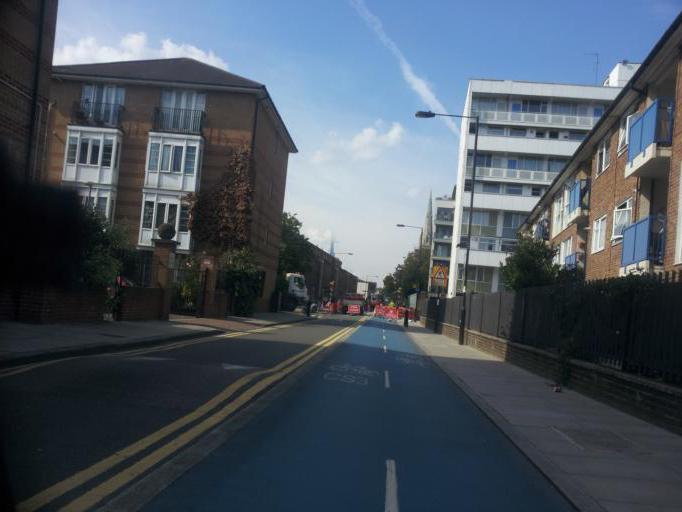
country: GB
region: England
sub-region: Greater London
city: Bethnal Green
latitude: 51.5115
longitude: -0.0472
